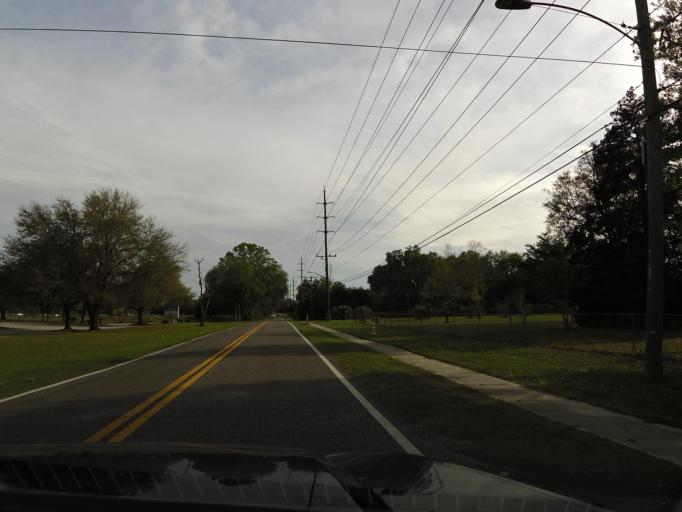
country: US
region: Florida
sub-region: Clay County
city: Bellair-Meadowbrook Terrace
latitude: 30.2308
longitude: -81.7644
